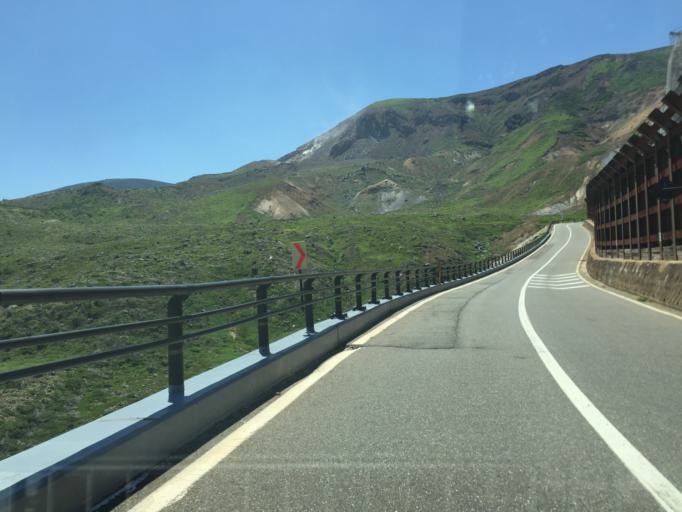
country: JP
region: Fukushima
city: Fukushima-shi
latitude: 37.7317
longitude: 140.2656
